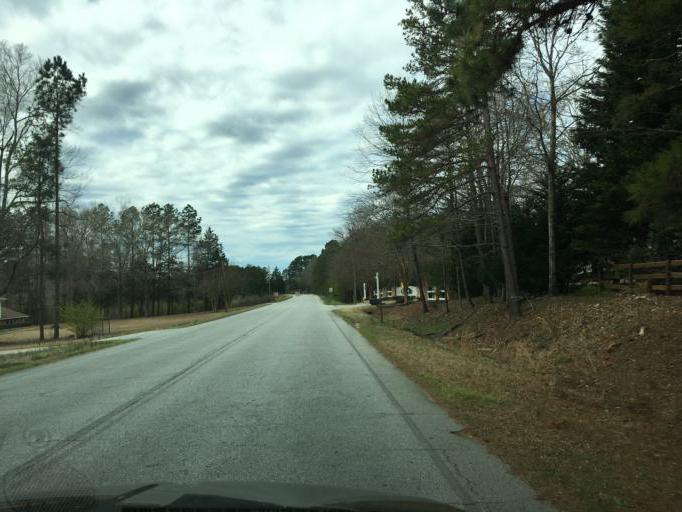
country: US
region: South Carolina
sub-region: Greenville County
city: Fountain Inn
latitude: 34.6776
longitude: -82.2215
